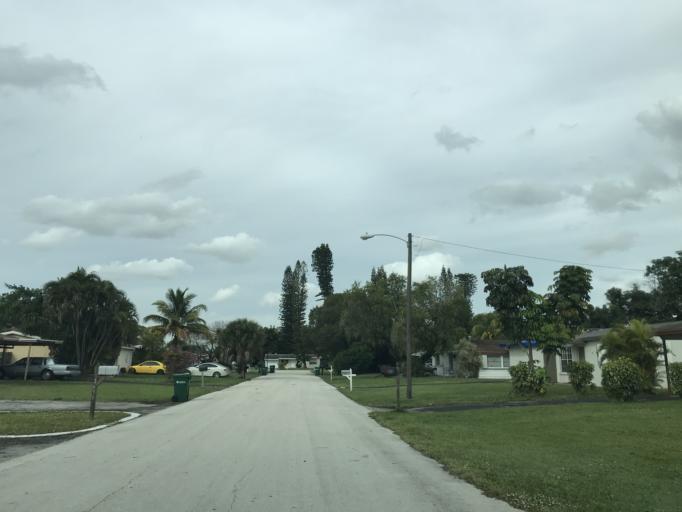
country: US
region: Florida
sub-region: Broward County
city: Margate
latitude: 26.2593
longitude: -80.2093
